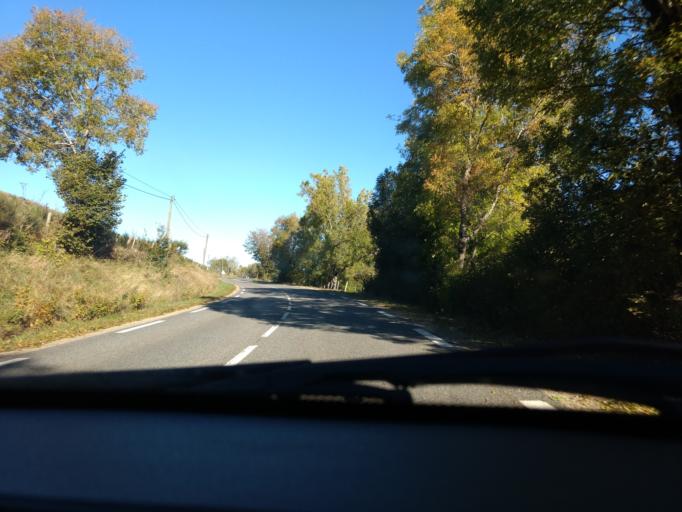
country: FR
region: Midi-Pyrenees
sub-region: Departement de l'Aveyron
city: Laguiole
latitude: 44.7014
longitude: 2.8643
